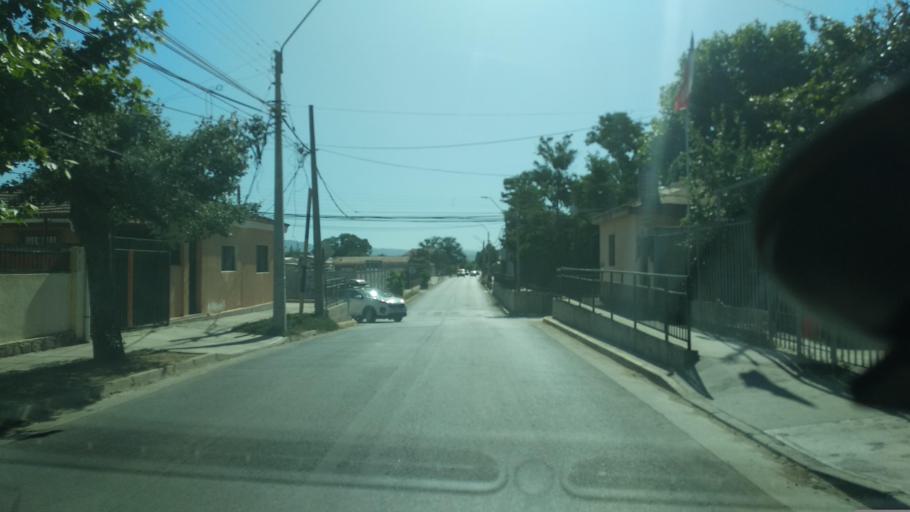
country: CL
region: Valparaiso
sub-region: Provincia de Marga Marga
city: Villa Alemana
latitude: -33.0434
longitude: -71.3858
